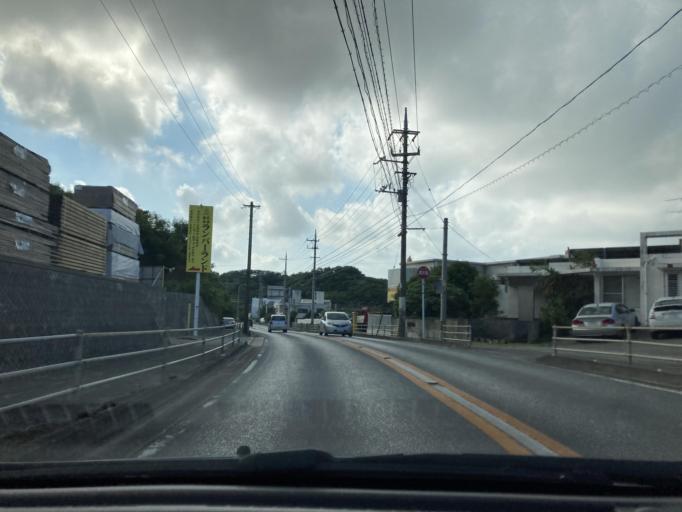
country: JP
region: Okinawa
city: Tomigusuku
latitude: 26.1612
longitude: 127.7404
